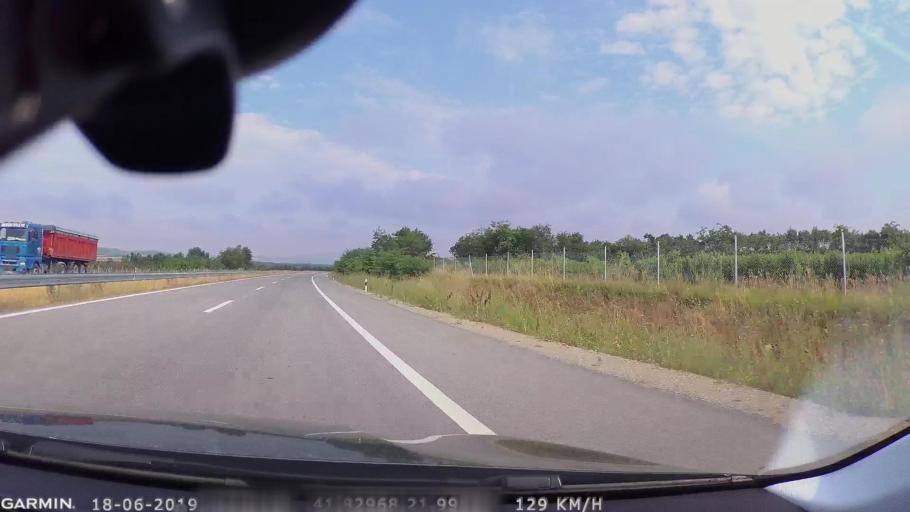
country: MK
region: Sveti Nikole
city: Sveti Nikole
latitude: 41.8299
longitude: 21.9981
